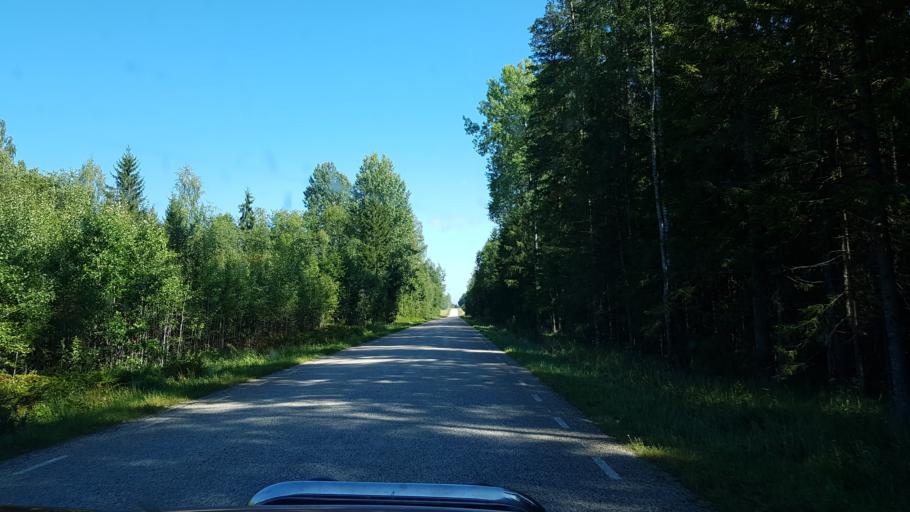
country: EE
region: Polvamaa
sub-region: Raepina vald
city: Rapina
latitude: 58.2260
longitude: 27.2959
